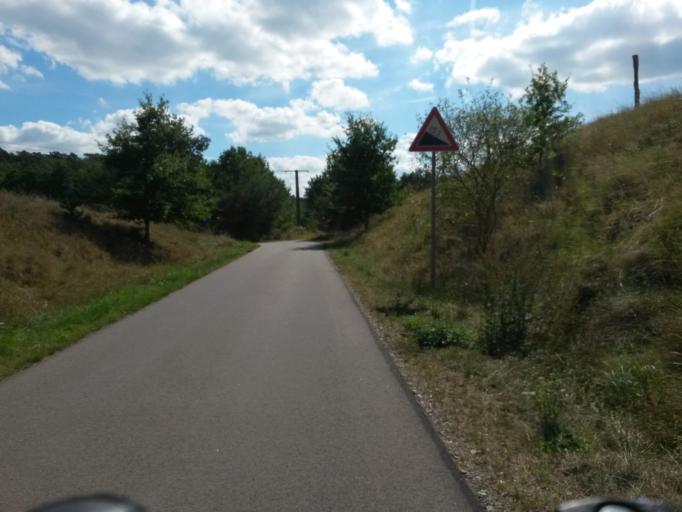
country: DE
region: Brandenburg
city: Templin
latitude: 53.1499
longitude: 13.5334
